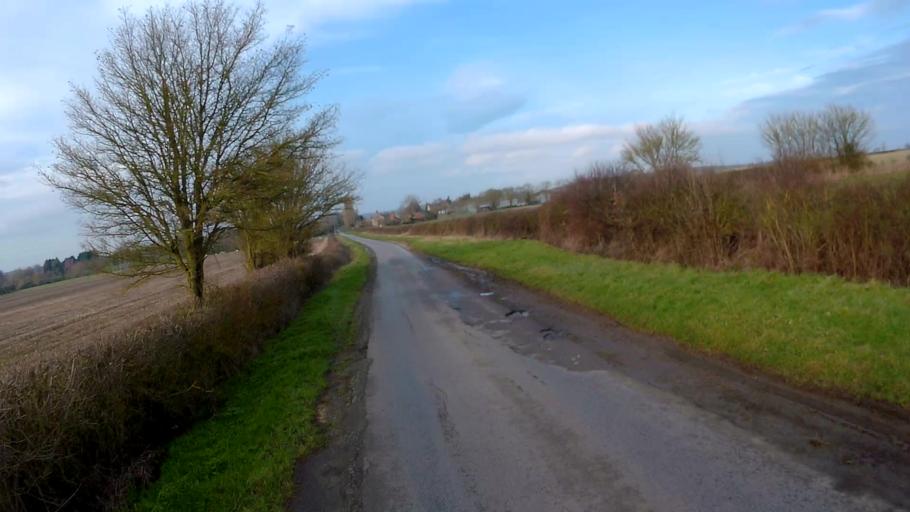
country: GB
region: England
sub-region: Lincolnshire
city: Bourne
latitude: 52.7395
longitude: -0.4028
